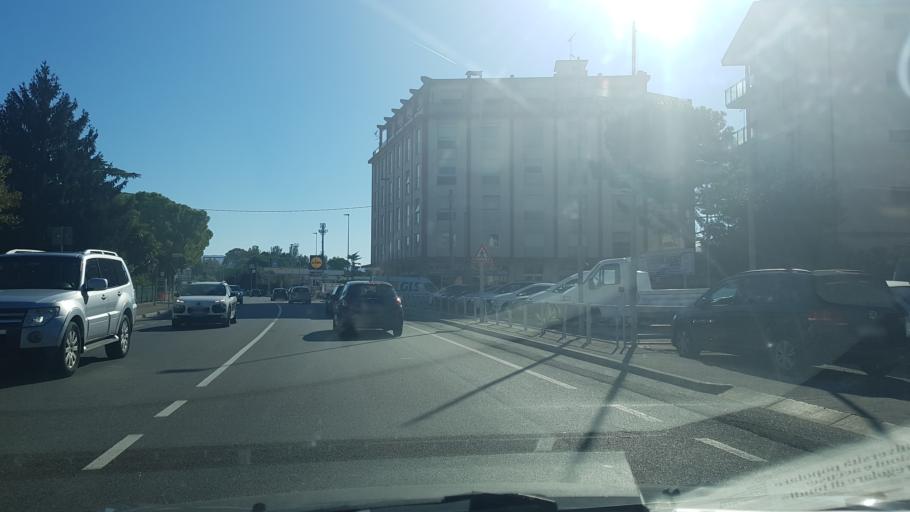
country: IT
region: Friuli Venezia Giulia
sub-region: Provincia di Gorizia
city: Monfalcone
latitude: 45.8028
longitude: 13.5394
